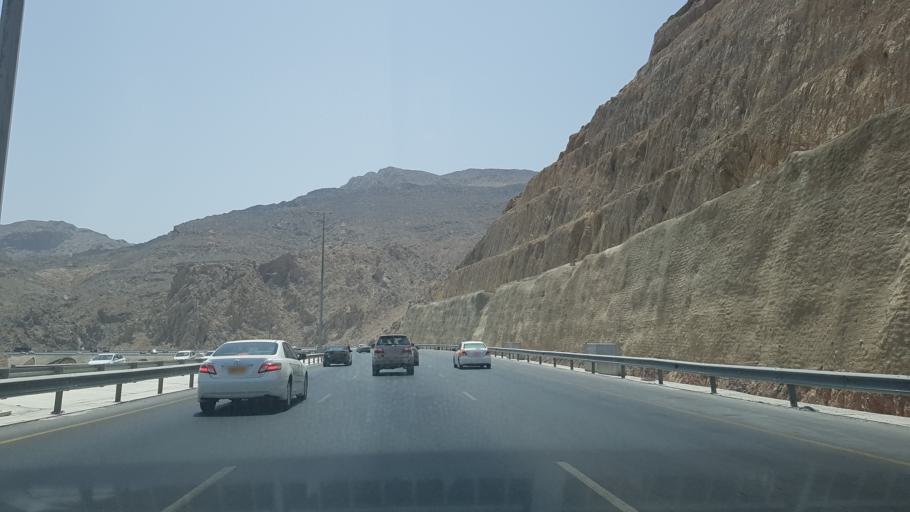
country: OM
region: Muhafazat Masqat
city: Muscat
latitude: 23.5698
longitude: 58.5229
